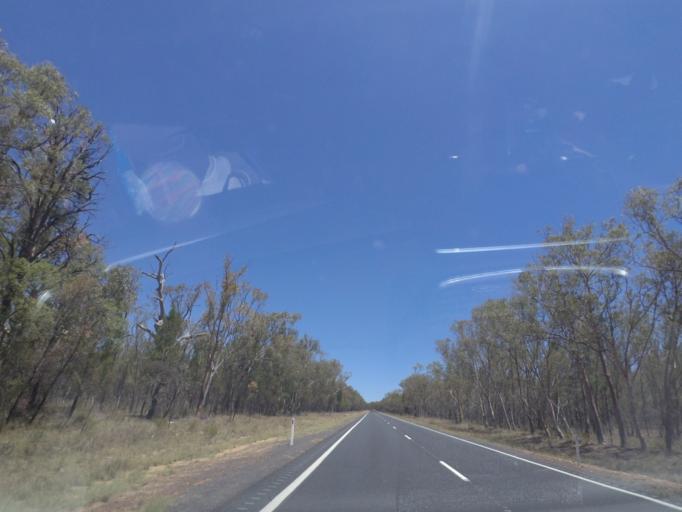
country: AU
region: New South Wales
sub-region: Warrumbungle Shire
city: Coonabarabran
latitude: -31.1732
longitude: 149.3596
